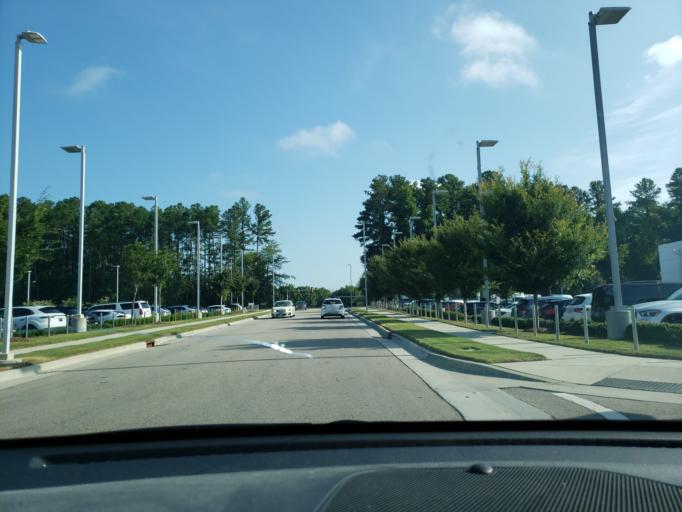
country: US
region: North Carolina
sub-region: Durham County
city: Durham
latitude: 35.8995
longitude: -78.9425
